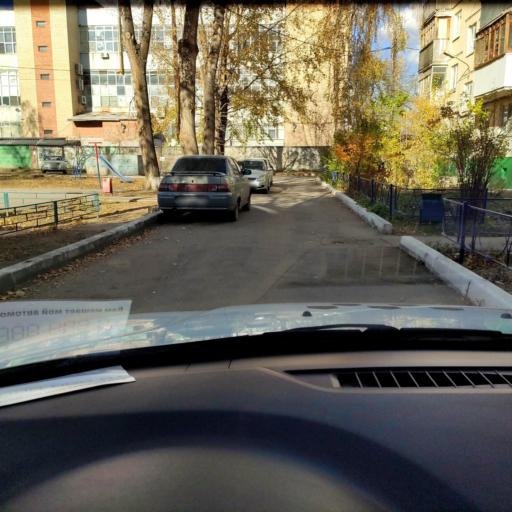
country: RU
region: Samara
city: Tol'yatti
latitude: 53.5114
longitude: 49.4315
